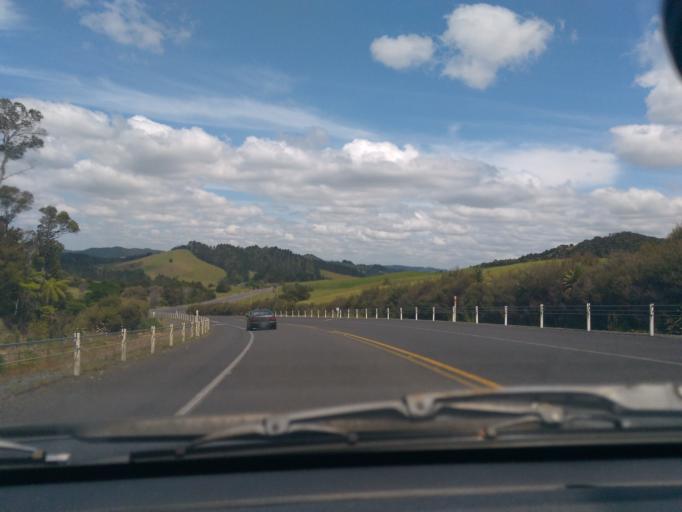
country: NZ
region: Northland
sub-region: Far North District
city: Kerikeri
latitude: -35.2754
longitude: 173.9494
